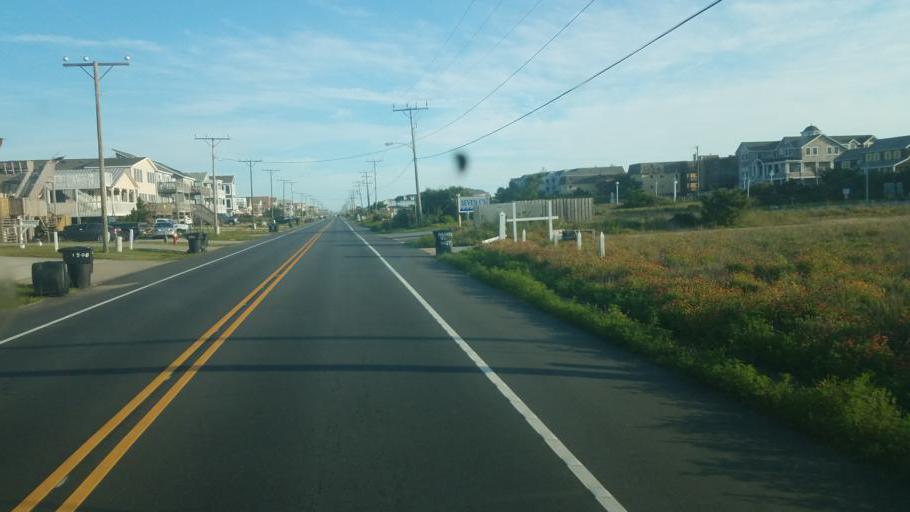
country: US
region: North Carolina
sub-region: Dare County
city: Kill Devil Hills
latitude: 36.0275
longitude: -75.6654
